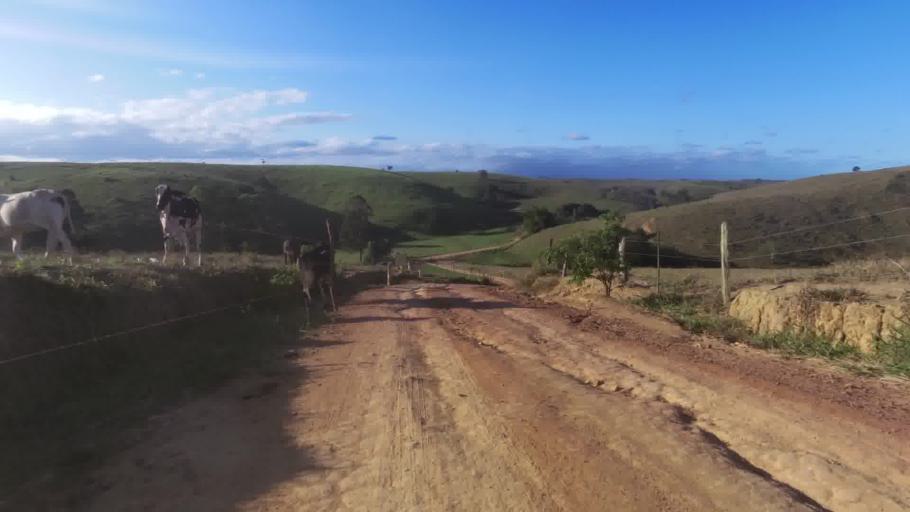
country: BR
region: Espirito Santo
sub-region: Marataizes
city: Marataizes
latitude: -21.1513
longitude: -41.0332
